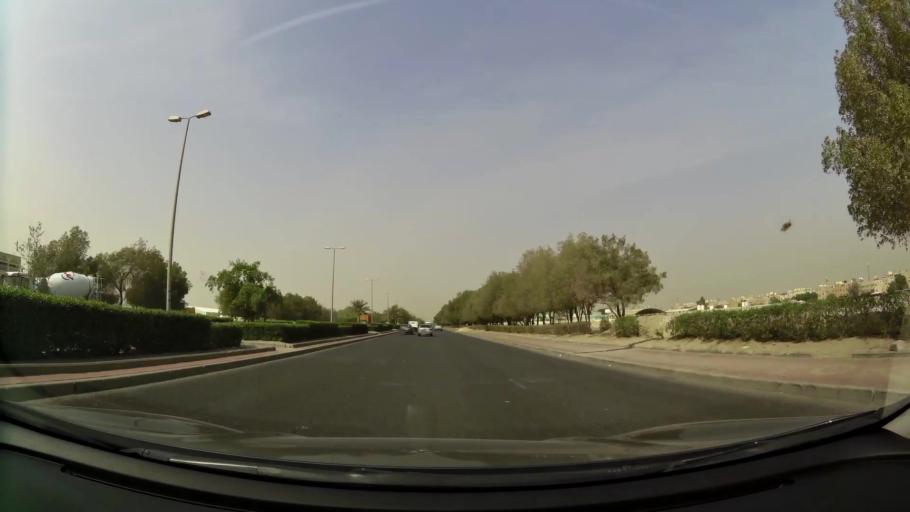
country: KW
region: Al Asimah
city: Ar Rabiyah
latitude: 29.2562
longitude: 47.9184
